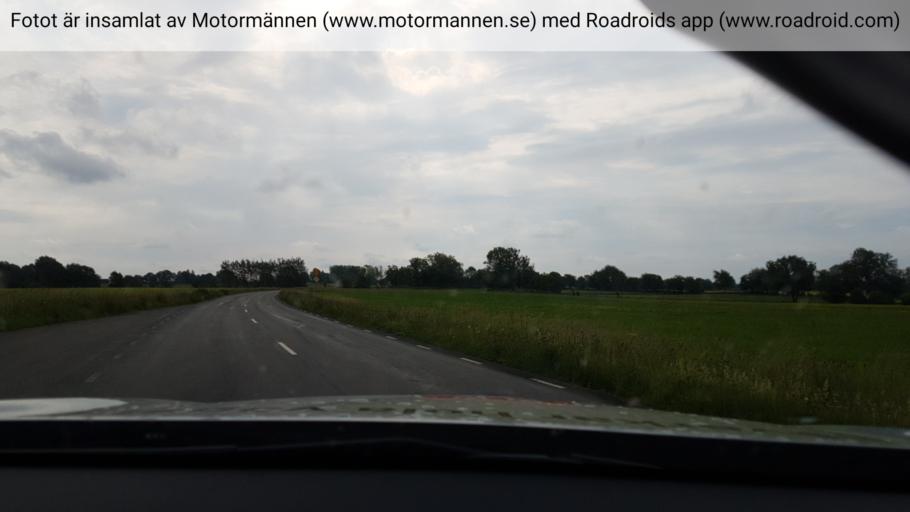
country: SE
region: Vaestra Goetaland
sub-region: Skovde Kommun
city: Skultorp
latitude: 58.3327
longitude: 13.7733
